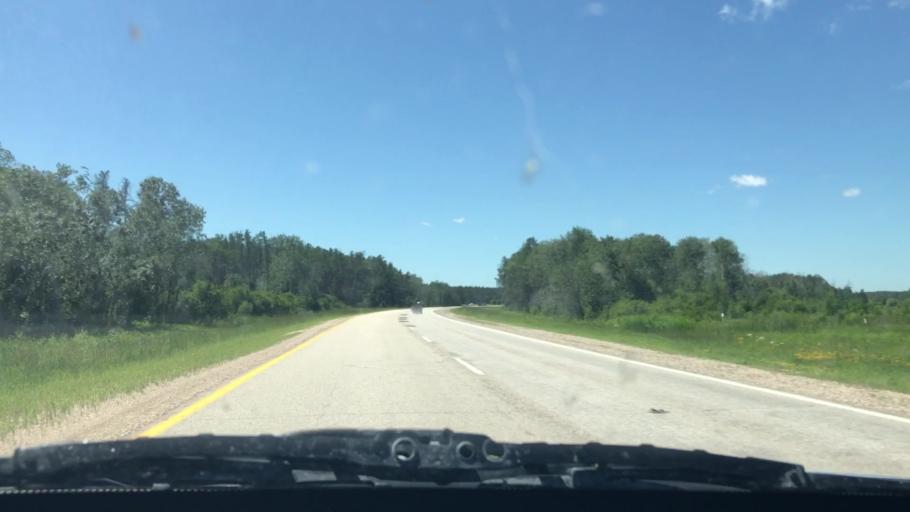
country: CA
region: Manitoba
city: La Broquerie
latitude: 49.6576
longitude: -96.1433
